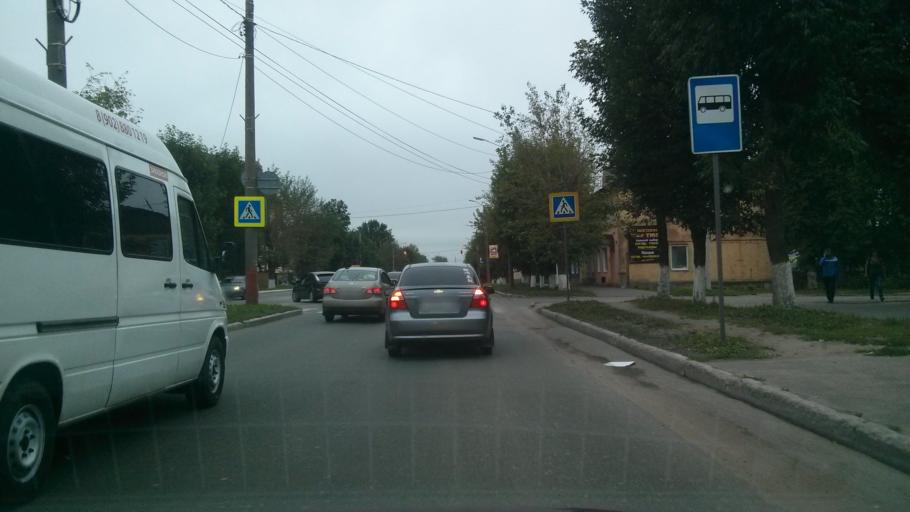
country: RU
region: Vladimir
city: Murom
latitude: 55.5694
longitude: 42.0397
